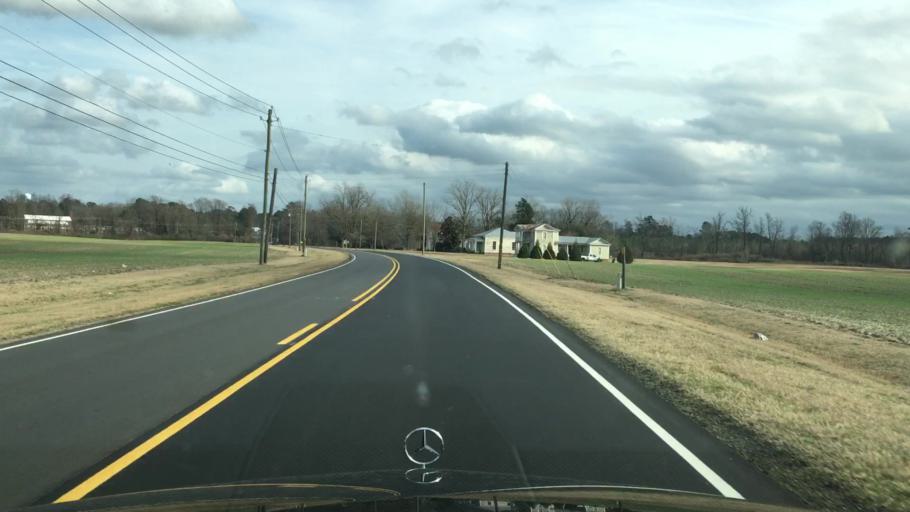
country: US
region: North Carolina
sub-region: Duplin County
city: Kenansville
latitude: 34.9588
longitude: -77.9837
